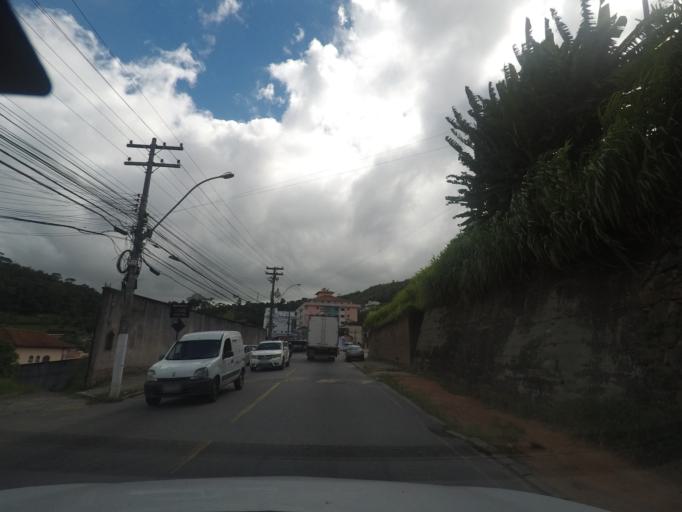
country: BR
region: Rio de Janeiro
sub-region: Teresopolis
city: Teresopolis
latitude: -22.4005
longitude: -42.9628
